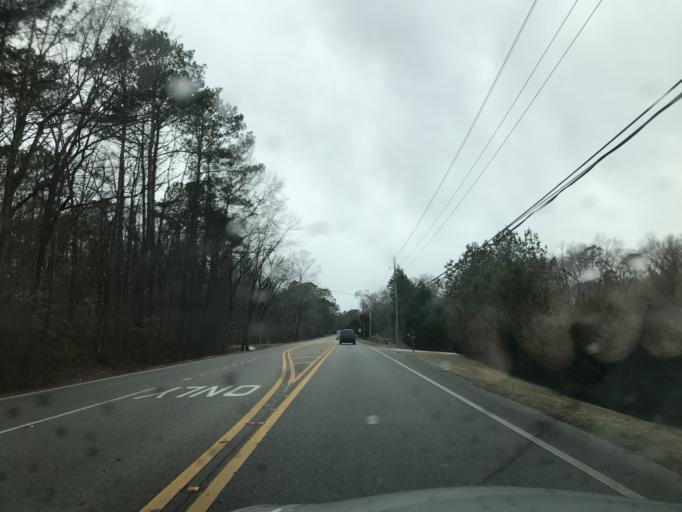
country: US
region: Alabama
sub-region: Shelby County
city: Meadowbrook
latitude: 33.3755
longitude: -86.7170
